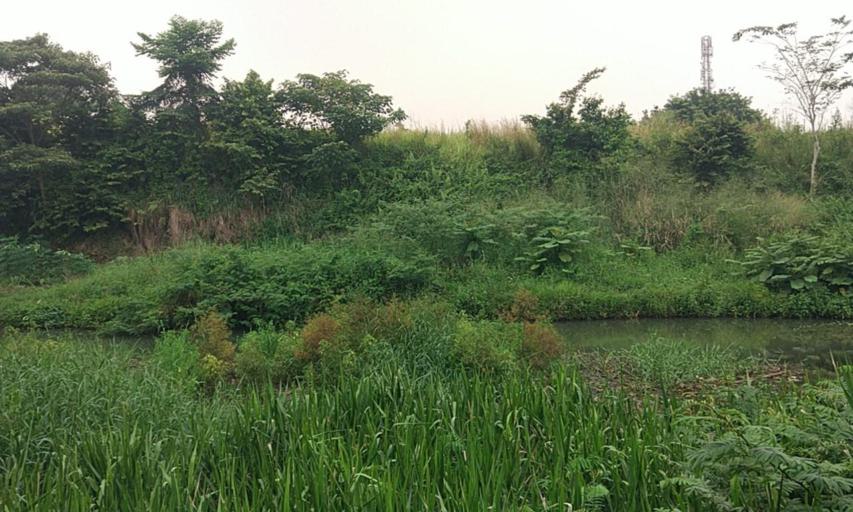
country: ID
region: West Java
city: Ciampea
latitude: -6.5133
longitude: 106.7706
